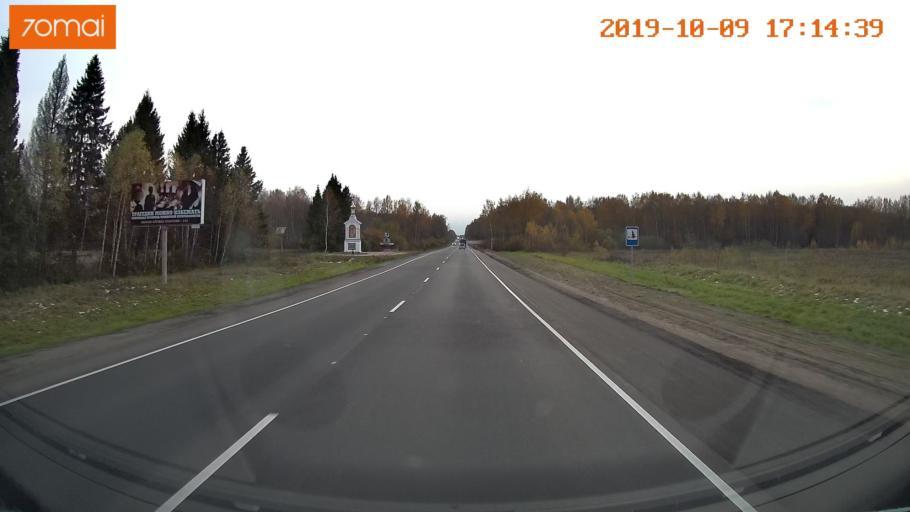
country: RU
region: Ivanovo
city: Furmanov
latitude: 57.3038
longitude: 41.2068
